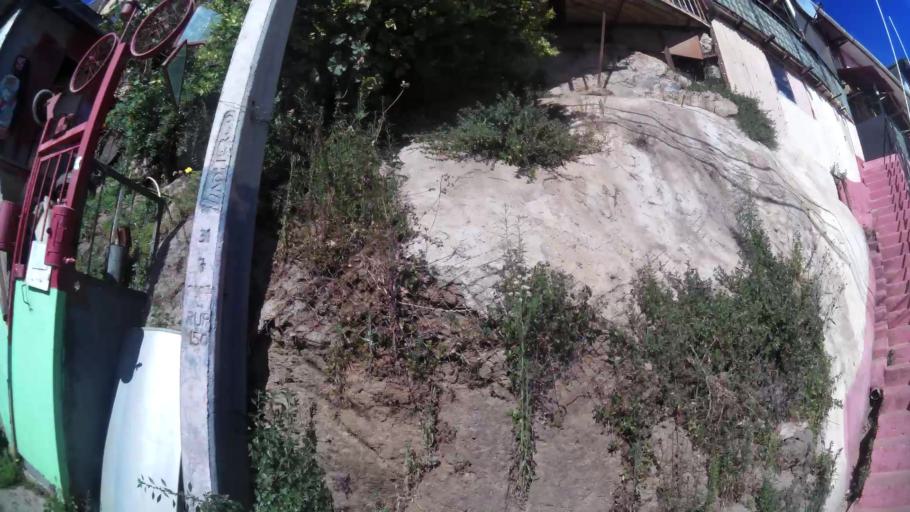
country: CL
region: Valparaiso
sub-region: Provincia de Valparaiso
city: Valparaiso
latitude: -33.0464
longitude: -71.6401
